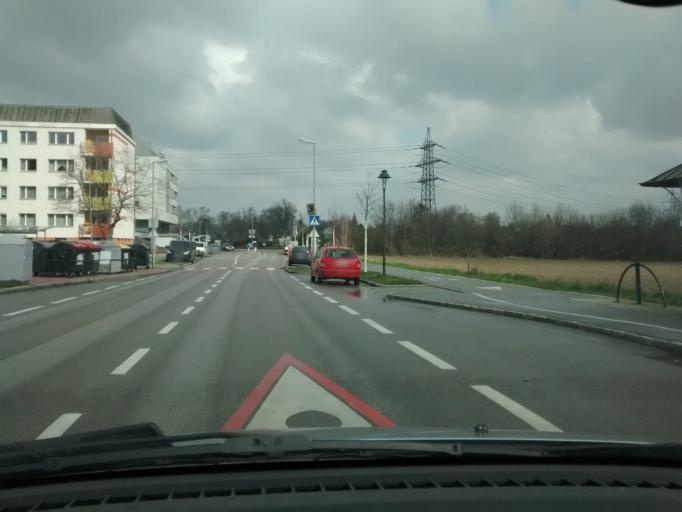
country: AT
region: Lower Austria
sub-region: Politischer Bezirk Modling
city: Laxenburg
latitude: 48.0771
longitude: 16.3525
